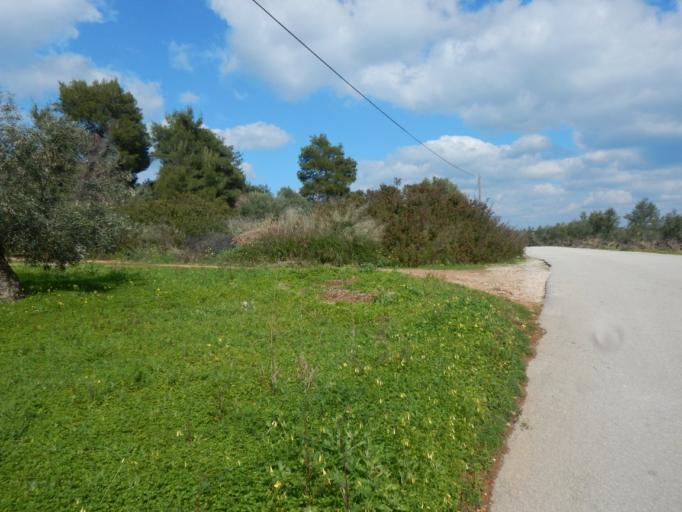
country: GR
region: Attica
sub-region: Nomarchia Anatolikis Attikis
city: Markopoulo Oropou
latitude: 38.2950
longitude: 23.8456
